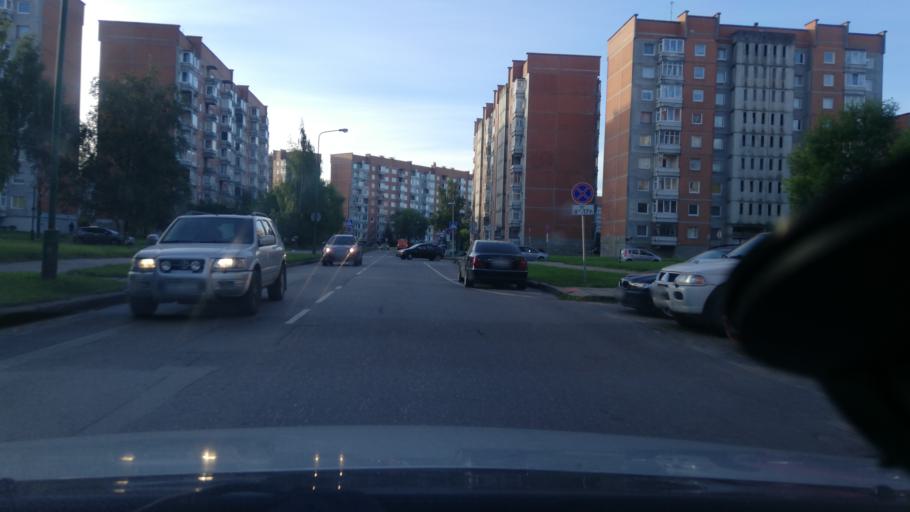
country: LT
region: Klaipedos apskritis
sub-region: Klaipeda
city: Klaipeda
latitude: 55.6687
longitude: 21.2006
